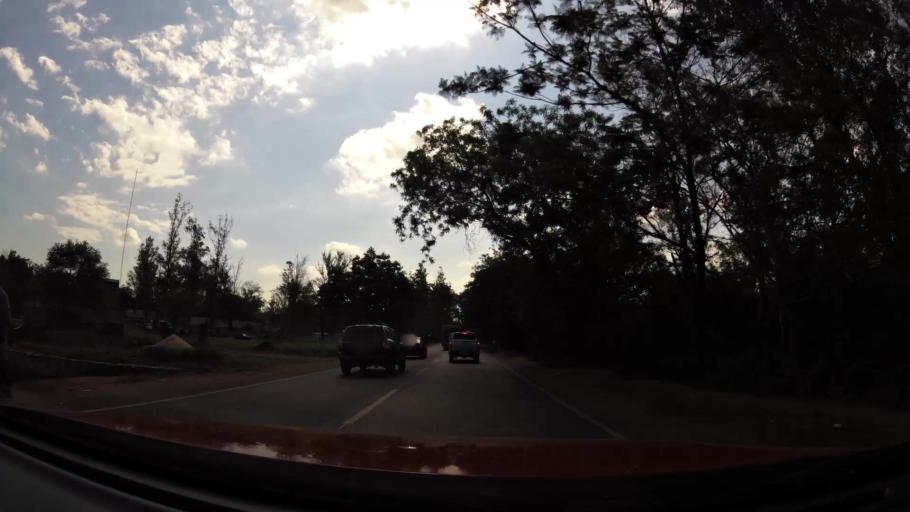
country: PY
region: Central
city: Fernando de la Mora
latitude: -25.3411
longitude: -57.5176
